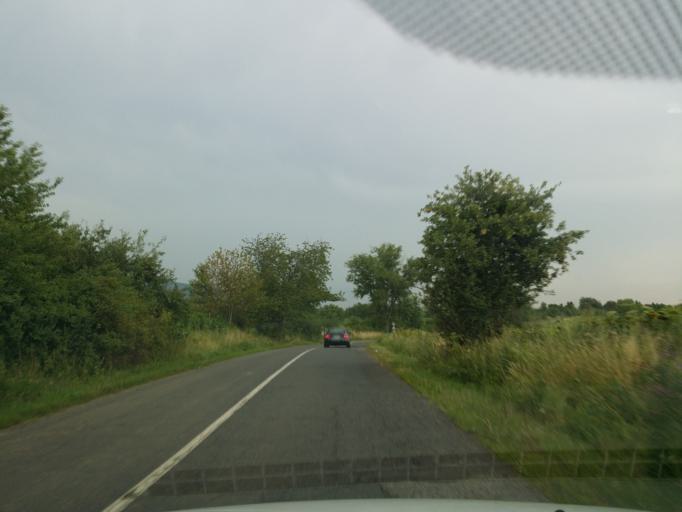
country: HU
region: Borsod-Abauj-Zemplen
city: Gonc
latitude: 48.4905
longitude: 21.2992
